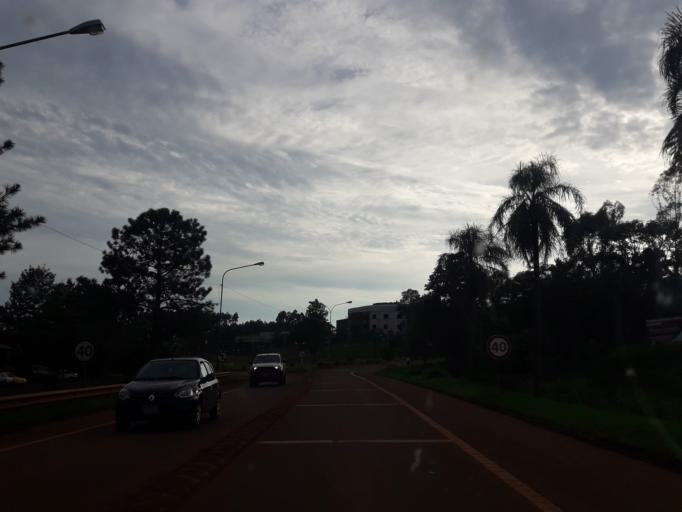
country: AR
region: Misiones
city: Dos de Mayo
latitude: -26.9890
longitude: -54.4801
